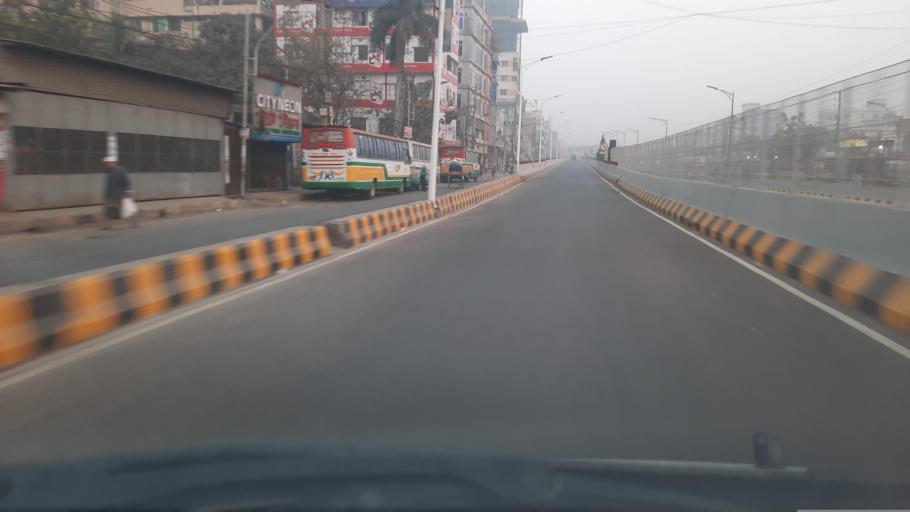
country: BD
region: Dhaka
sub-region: Dhaka
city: Dhaka
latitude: 23.7057
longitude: 90.4348
